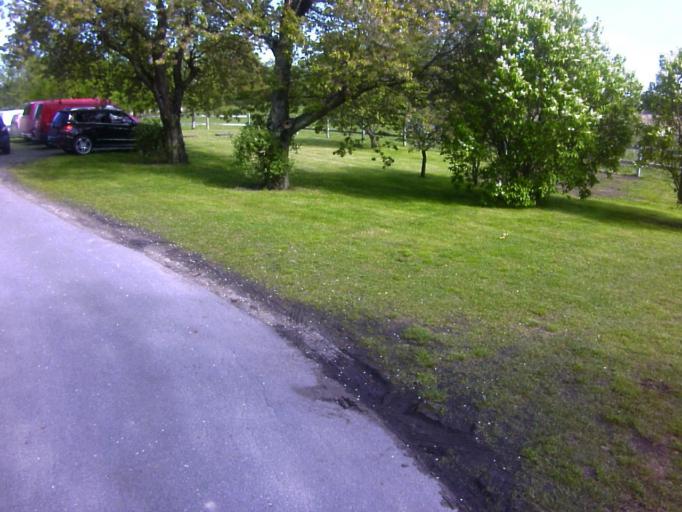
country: SE
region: Blekinge
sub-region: Solvesborgs Kommun
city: Soelvesborg
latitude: 56.0579
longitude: 14.6012
